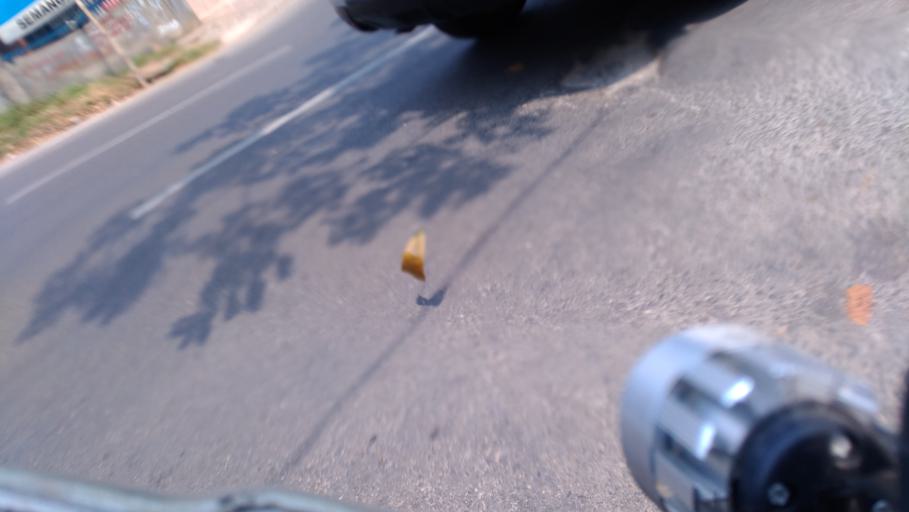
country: ID
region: West Java
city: Cileungsir
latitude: -6.3918
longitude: 106.9530
